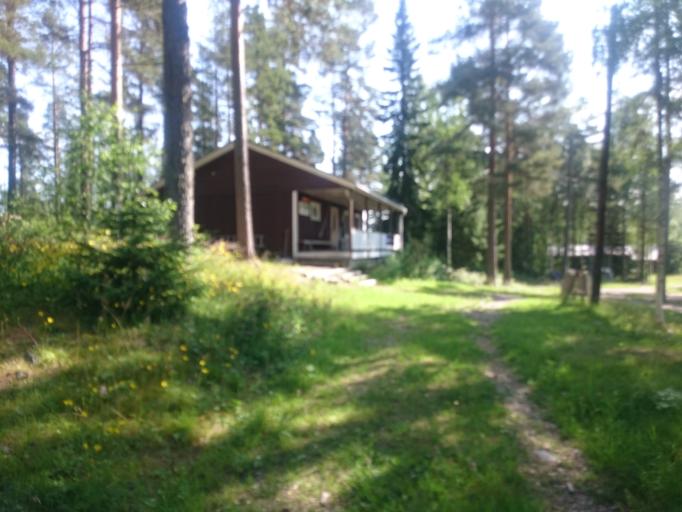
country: SE
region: Vaesternorrland
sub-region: OErnskoeldsviks Kommun
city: Bredbyn
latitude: 63.3019
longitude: 18.2588
